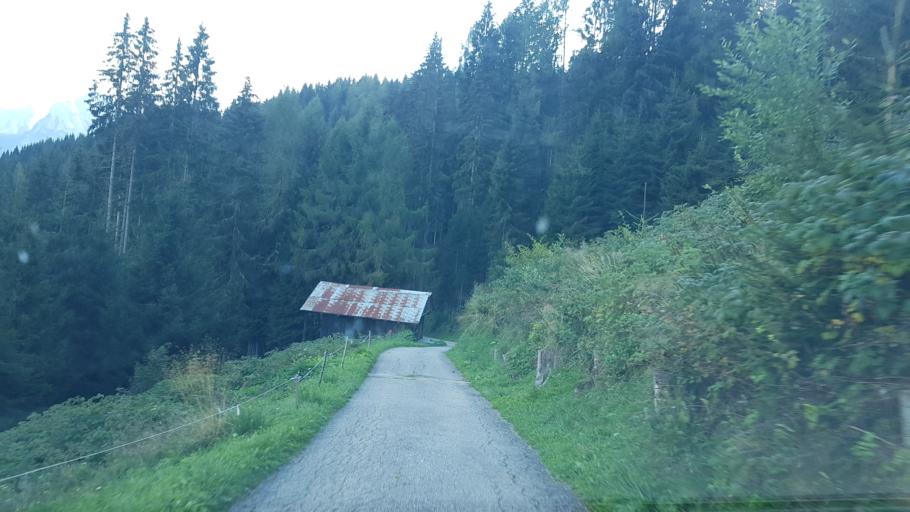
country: IT
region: Veneto
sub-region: Provincia di Belluno
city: San Pietro di Cadore
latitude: 46.5907
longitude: 12.5920
